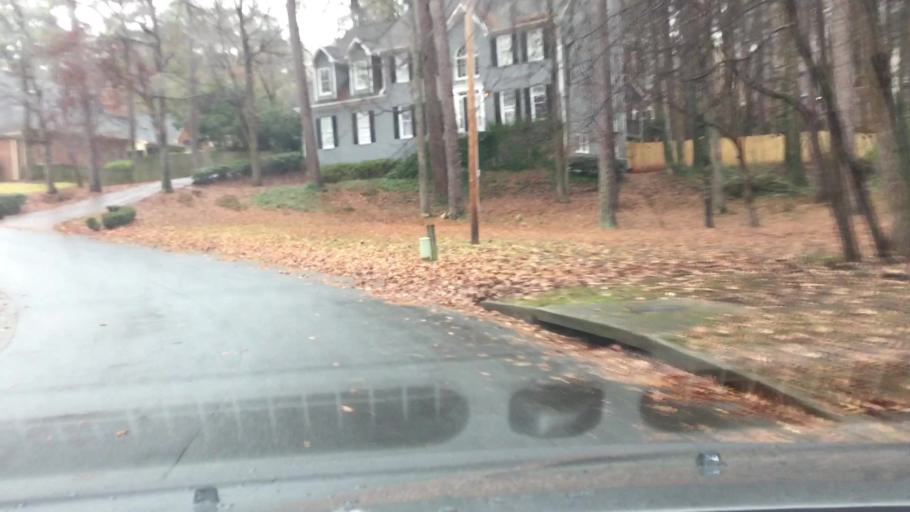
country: US
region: Georgia
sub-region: Cobb County
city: Fair Oaks
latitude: 33.9126
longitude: -84.6150
